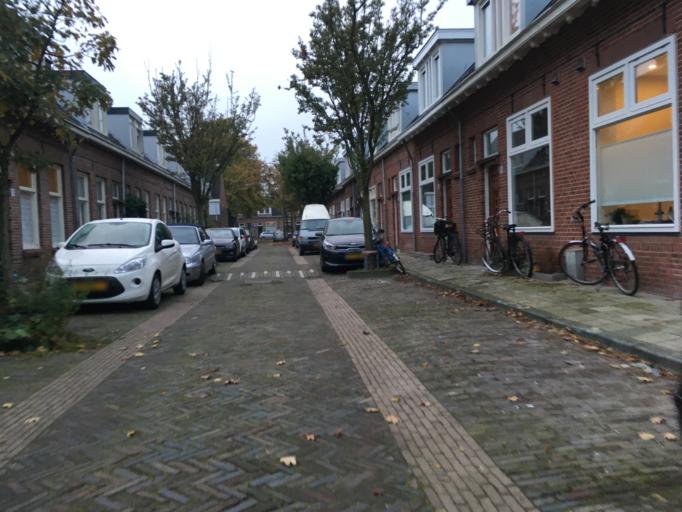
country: NL
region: North Holland
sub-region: Gemeente Haarlem
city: Haarlem
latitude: 52.3775
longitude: 4.6539
